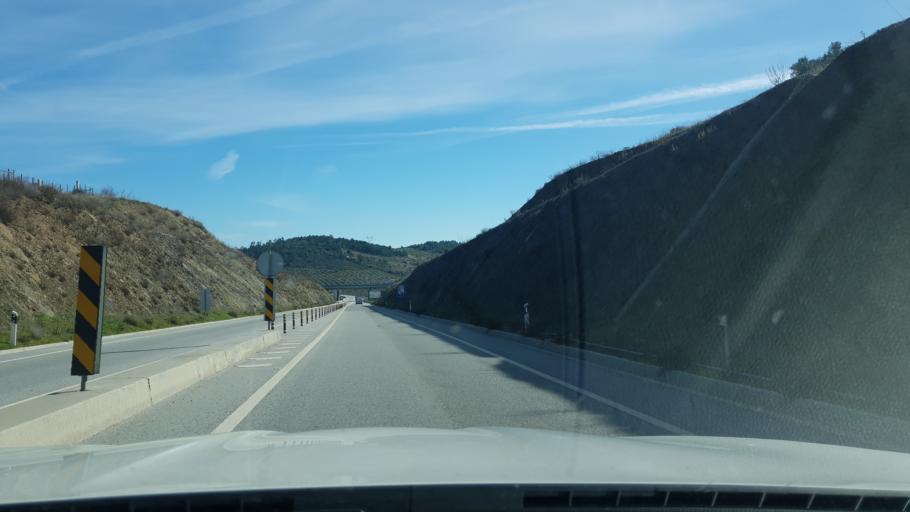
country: PT
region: Braganca
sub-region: Braganca Municipality
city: Vila Flor
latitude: 41.3011
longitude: -7.1499
